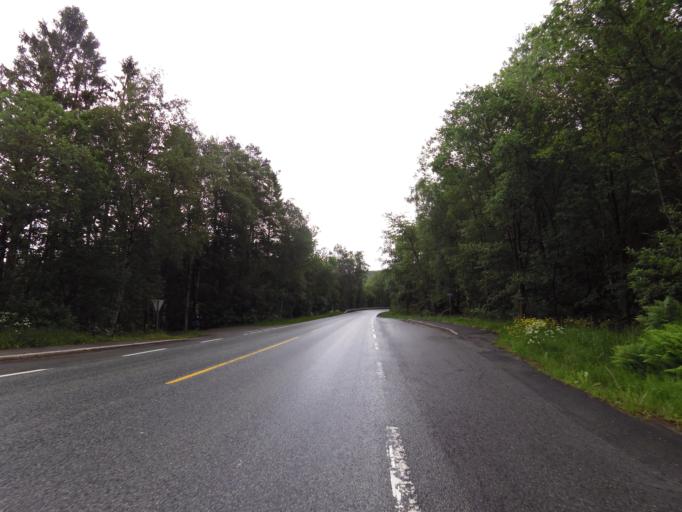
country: NO
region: Vest-Agder
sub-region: Farsund
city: Farsund
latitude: 58.1018
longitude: 6.8484
